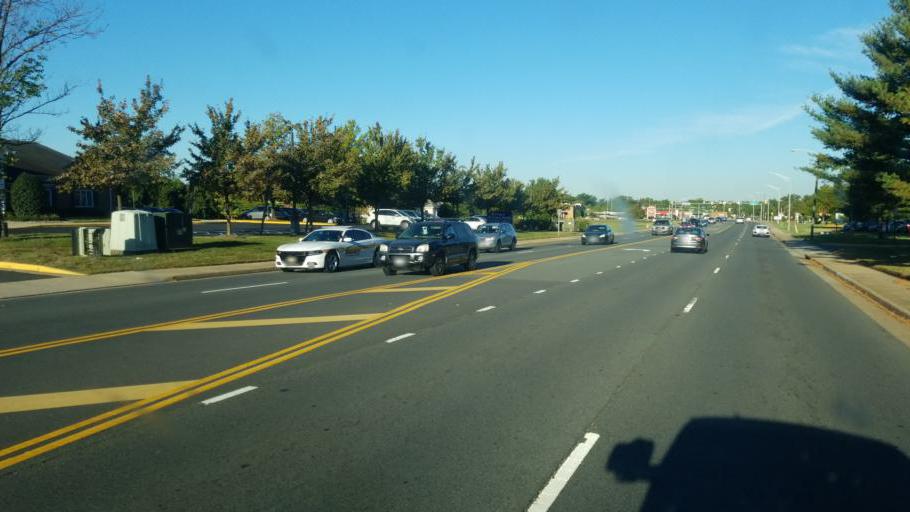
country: US
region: Virginia
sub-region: City of Manassas
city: Manassas
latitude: 38.7526
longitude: -77.4857
